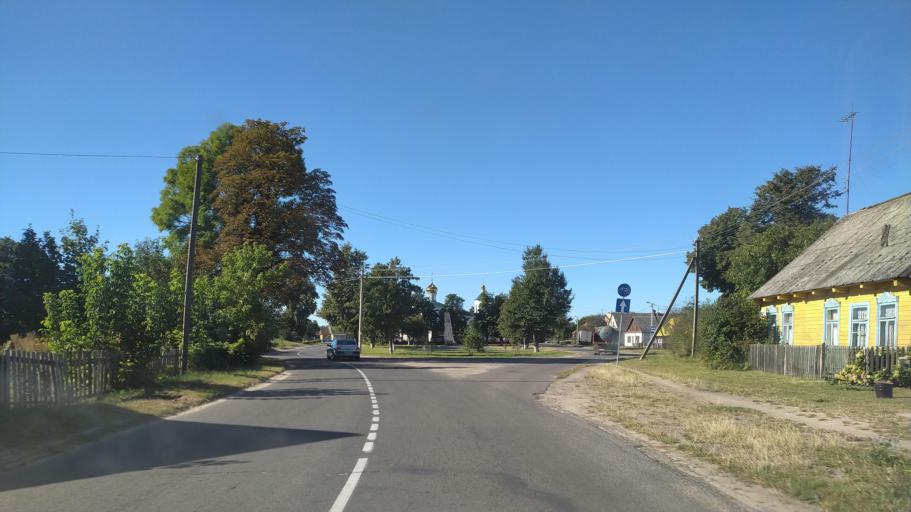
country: BY
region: Brest
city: Pruzhany
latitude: 52.4834
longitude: 24.7052
